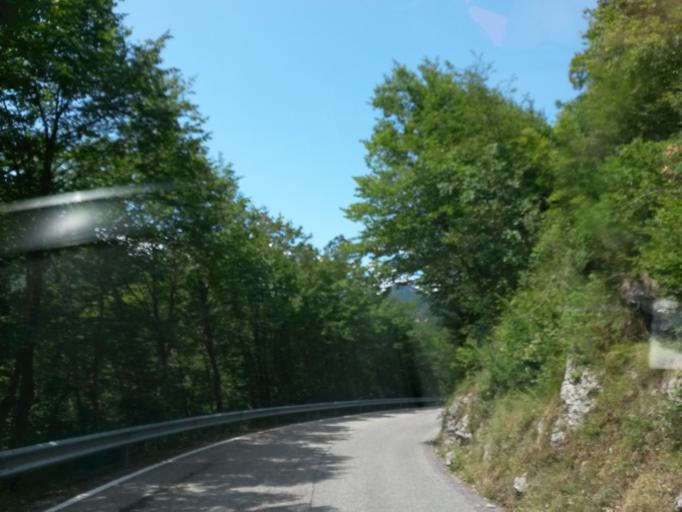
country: IT
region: Lombardy
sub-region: Provincia di Brescia
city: Gargnano
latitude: 45.6840
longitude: 10.6151
